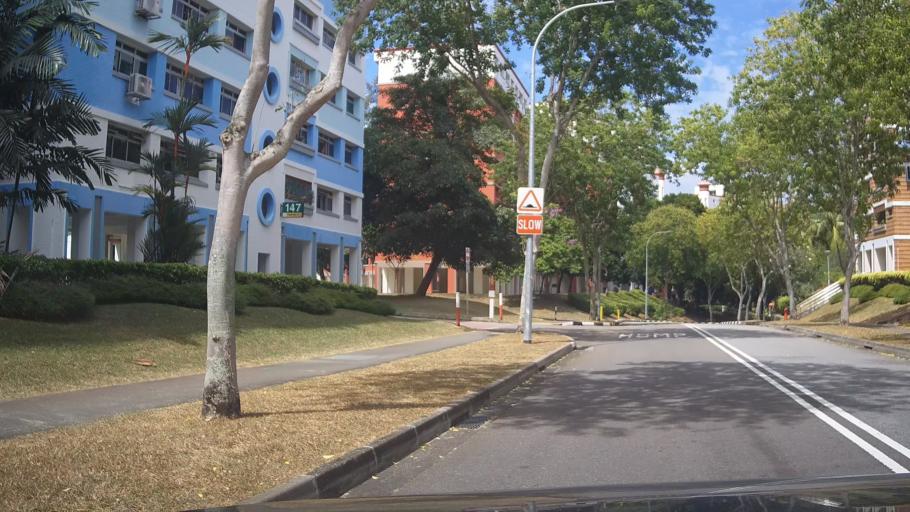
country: SG
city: Singapore
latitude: 1.3633
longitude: 103.9620
